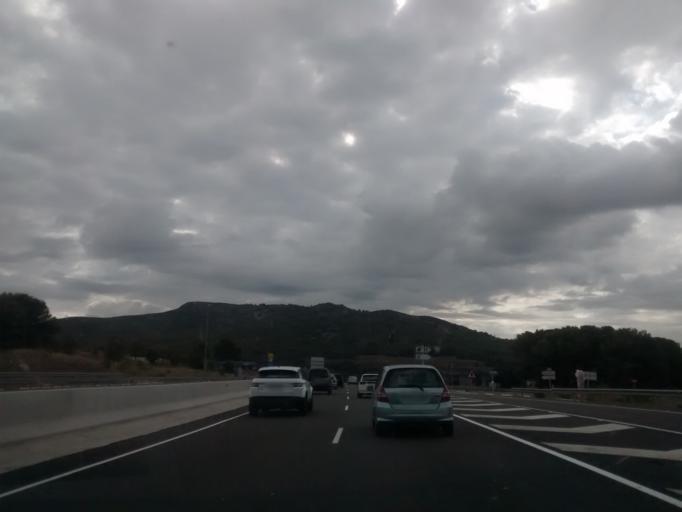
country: ES
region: Catalonia
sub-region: Provincia de Barcelona
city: Vilafranca del Penedes
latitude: 41.3233
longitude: 1.7161
